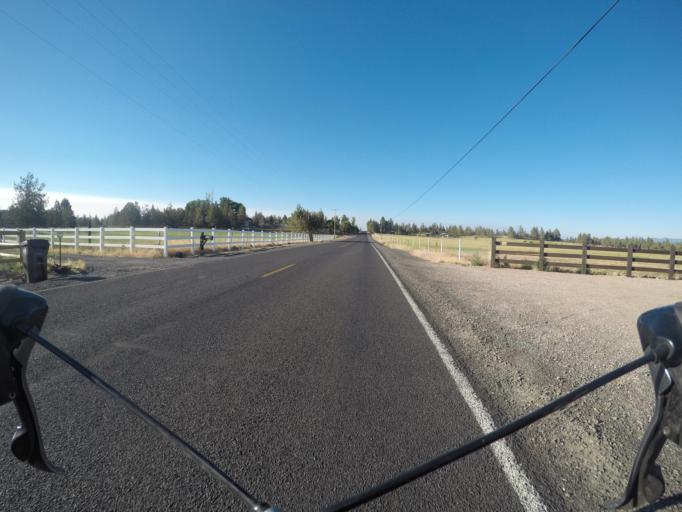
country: US
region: Oregon
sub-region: Deschutes County
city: Redmond
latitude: 44.2585
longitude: -121.2396
